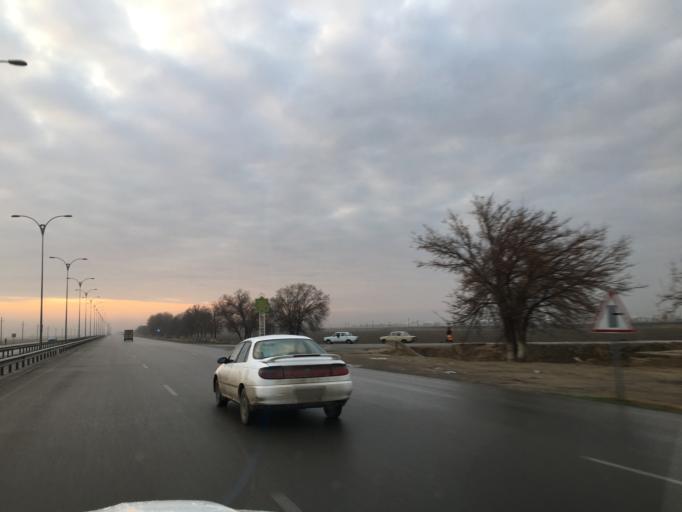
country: TM
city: Murgab
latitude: 37.5201
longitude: 61.9178
